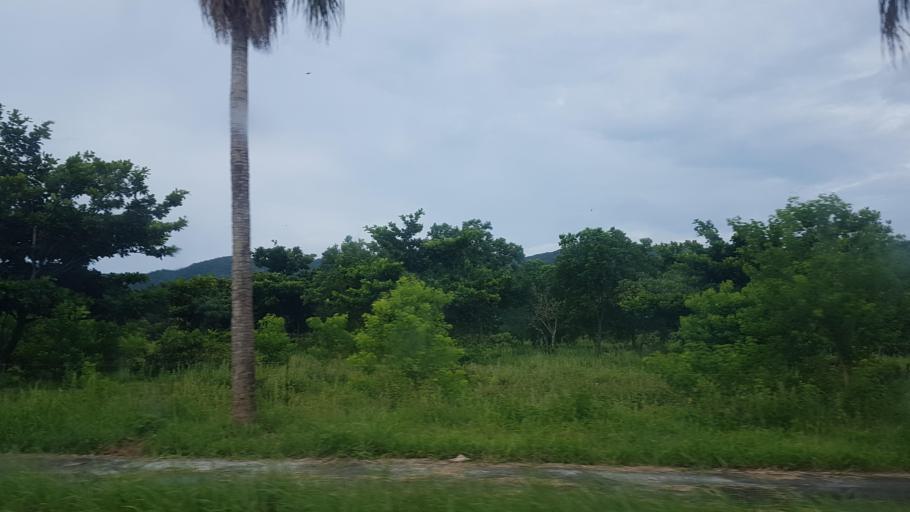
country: TW
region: Taiwan
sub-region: Hualien
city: Hualian
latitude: 23.8708
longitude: 121.5356
